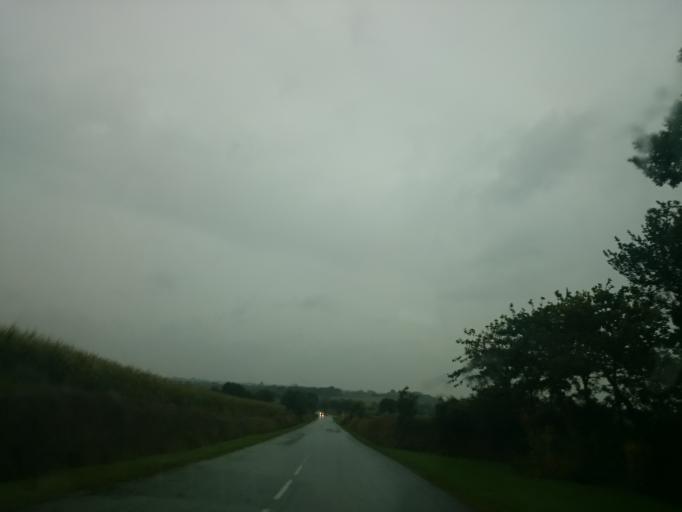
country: FR
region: Brittany
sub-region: Departement du Finistere
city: Plouvien
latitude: 48.5386
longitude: -4.4246
